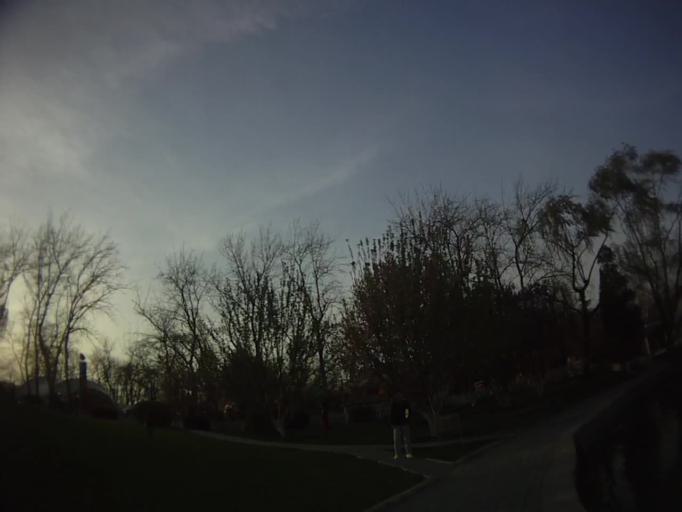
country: CN
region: Beijing
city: Longtan
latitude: 39.8775
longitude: 116.4312
